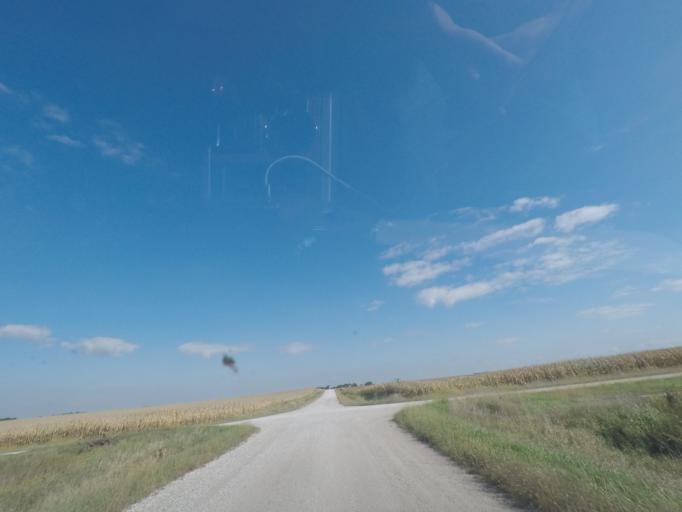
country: US
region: Iowa
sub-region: Story County
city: Nevada
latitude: 42.0487
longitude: -93.4252
